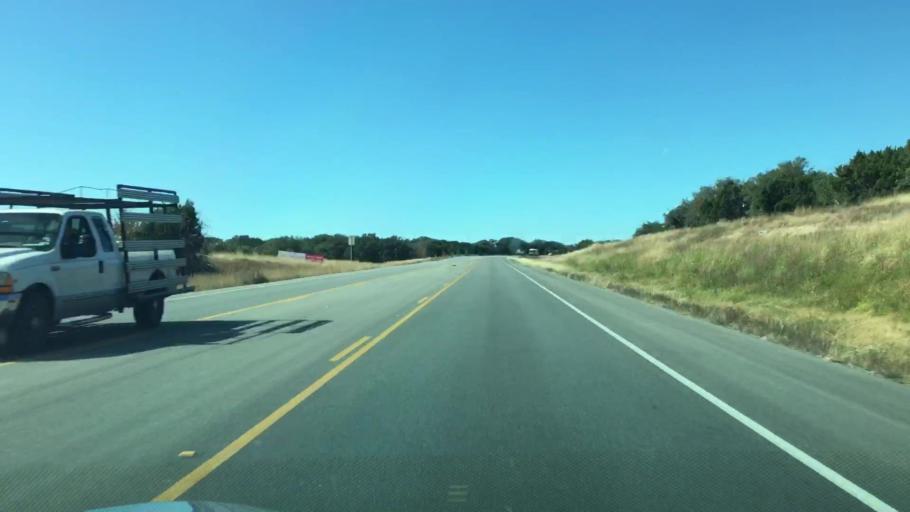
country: US
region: Texas
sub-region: Hays County
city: Dripping Springs
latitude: 30.2080
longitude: -98.1489
